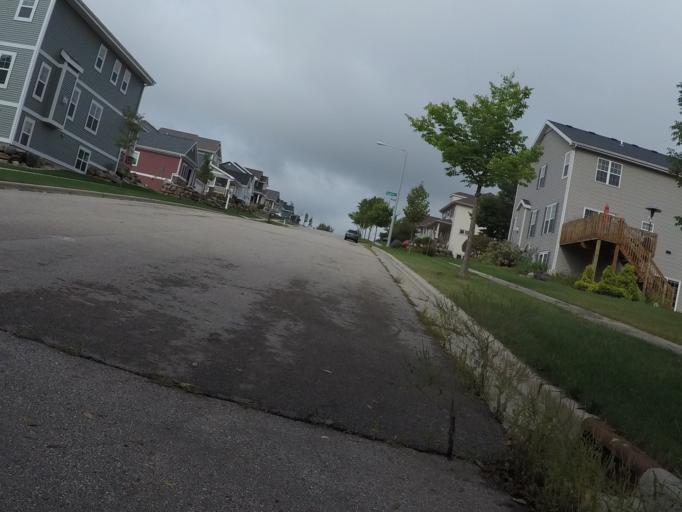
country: US
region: Wisconsin
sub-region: Dane County
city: Verona
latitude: 43.0432
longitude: -89.5378
